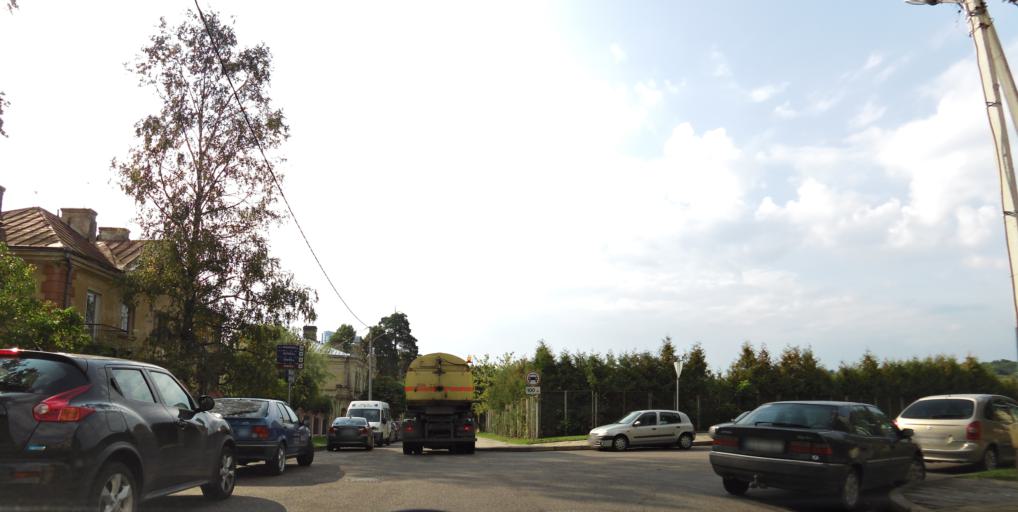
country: LT
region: Vilnius County
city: Naujamiestis
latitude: 54.6877
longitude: 25.2562
